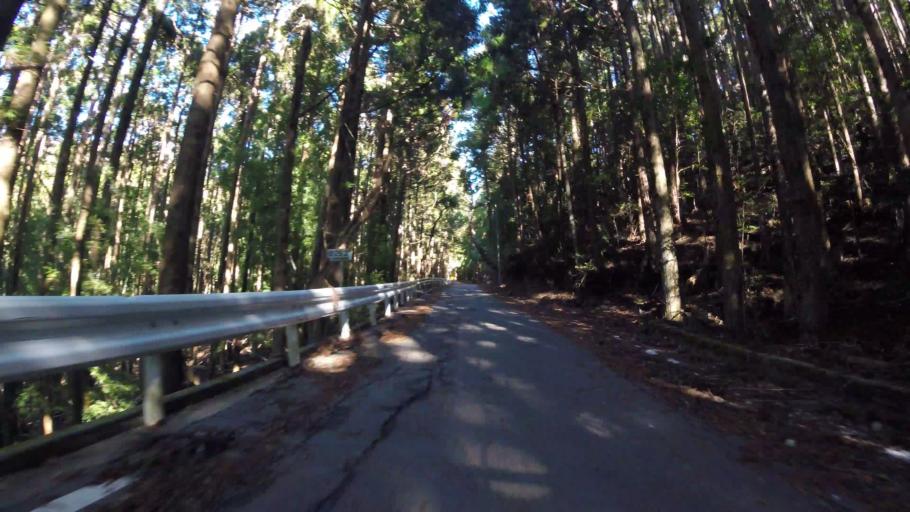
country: JP
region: Shizuoka
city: Ito
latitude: 34.8921
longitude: 138.9506
